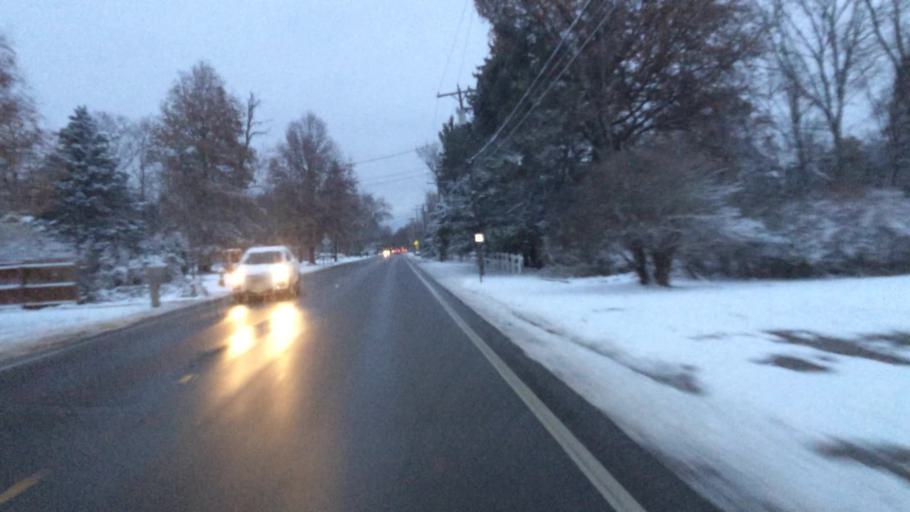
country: US
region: Ohio
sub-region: Cuyahoga County
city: Olmsted Falls
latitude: 41.3442
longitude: -81.9038
